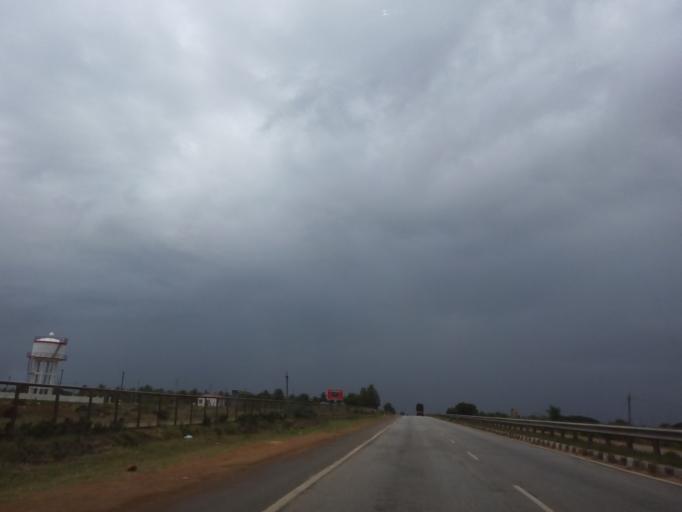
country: IN
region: Karnataka
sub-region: Davanagere
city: Harihar
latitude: 14.4608
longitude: 75.8550
